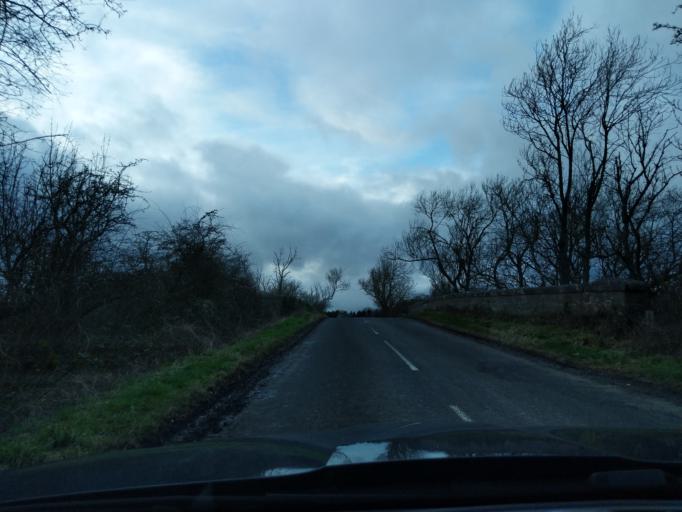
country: GB
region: England
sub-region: Northumberland
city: Ford
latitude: 55.7160
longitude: -2.1366
